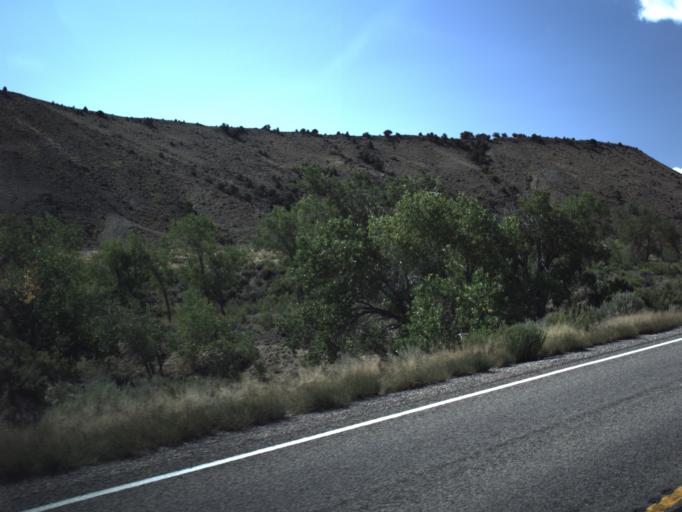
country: US
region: Utah
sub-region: Emery County
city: Ferron
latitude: 38.7911
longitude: -111.3480
